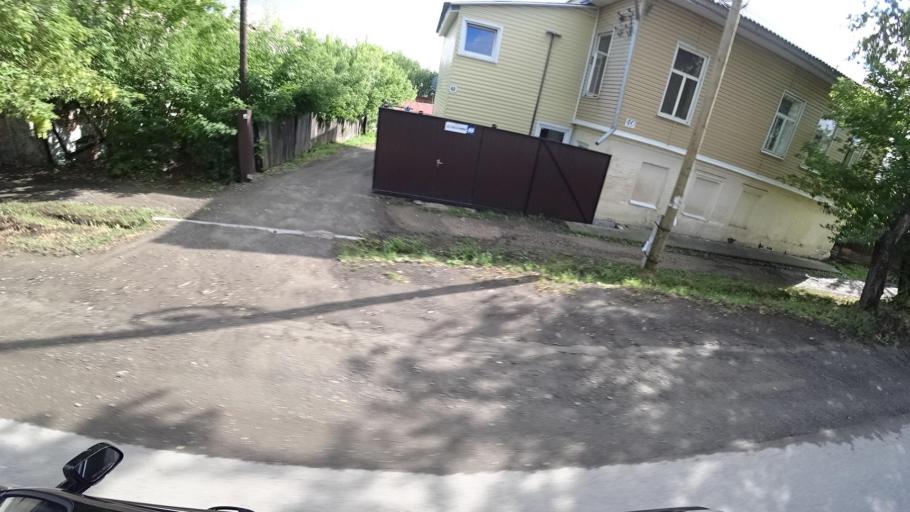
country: RU
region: Sverdlovsk
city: Kamyshlov
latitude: 56.8475
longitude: 62.7025
